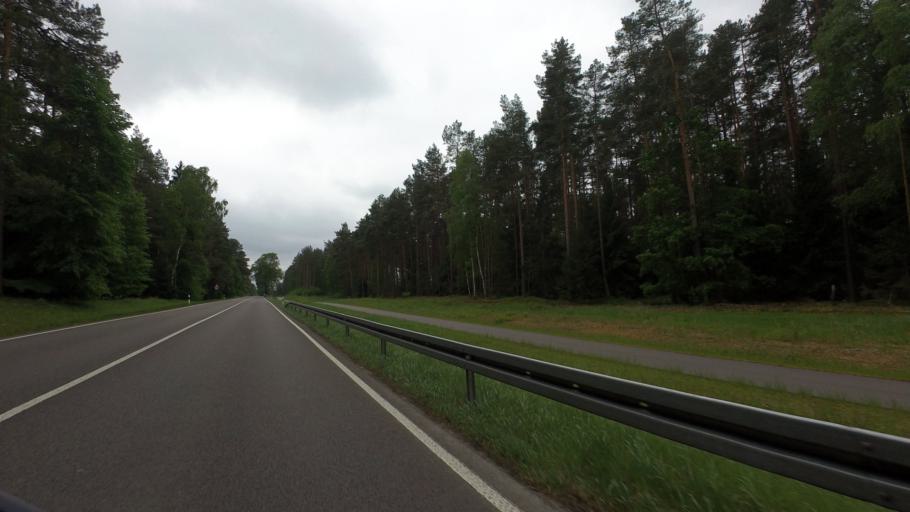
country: DE
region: Mecklenburg-Vorpommern
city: Neustrelitz
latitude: 53.2880
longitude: 13.1093
